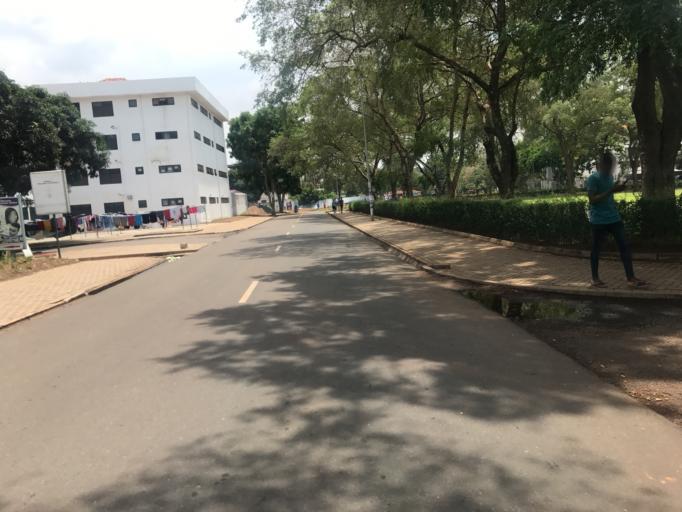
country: GH
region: Greater Accra
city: Medina Estates
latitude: 5.6460
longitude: -0.1858
